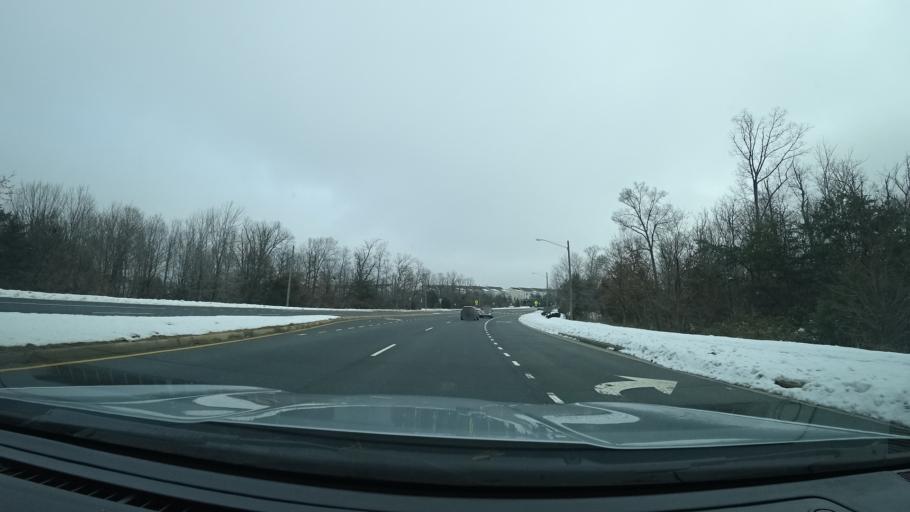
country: US
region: Virginia
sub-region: Fairfax County
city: Floris
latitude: 38.9456
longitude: -77.3969
